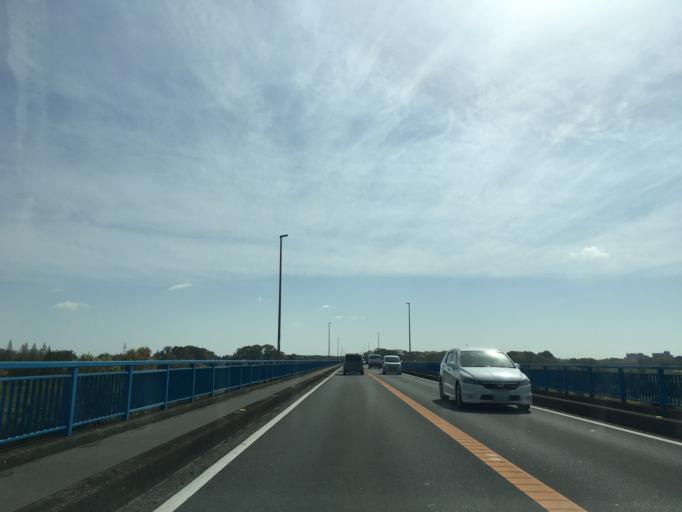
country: JP
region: Saitama
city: Okegawa
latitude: 35.9423
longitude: 139.5400
